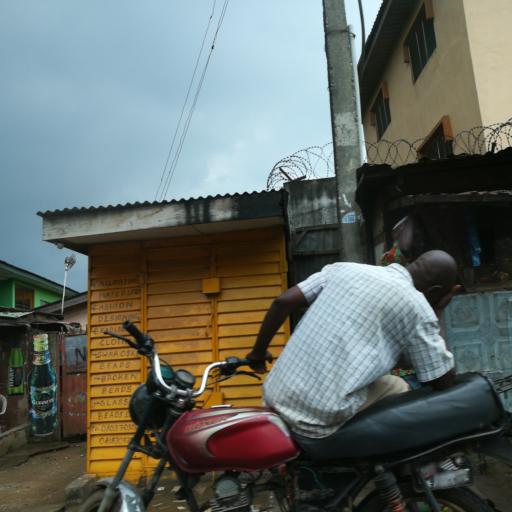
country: NG
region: Lagos
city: Agege
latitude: 6.5982
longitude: 3.2931
